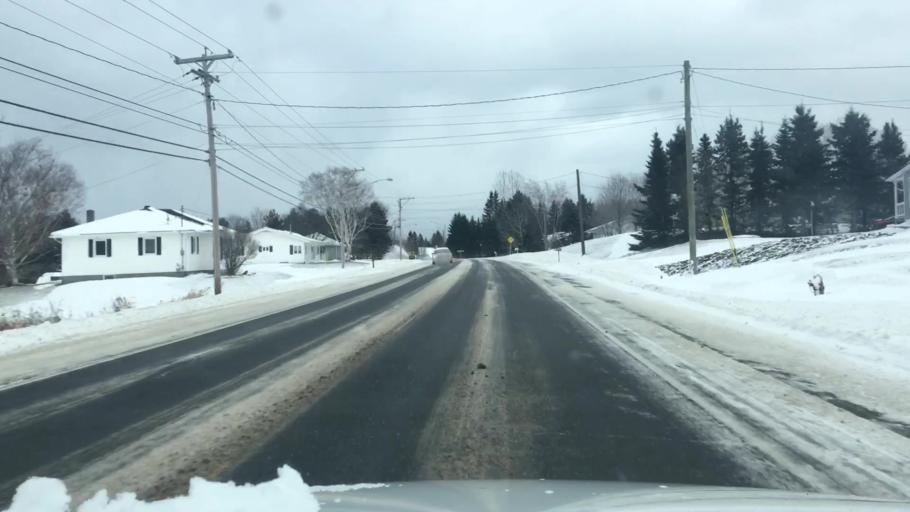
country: US
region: Maine
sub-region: Aroostook County
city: Madawaska
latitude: 47.3468
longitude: -68.2658
